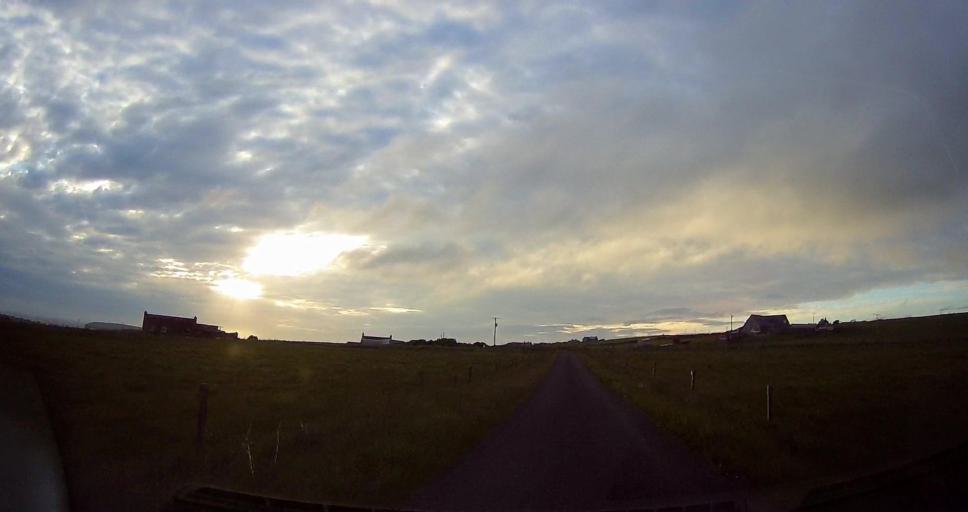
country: GB
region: Scotland
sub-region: Orkney Islands
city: Stromness
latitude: 59.1231
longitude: -3.2782
